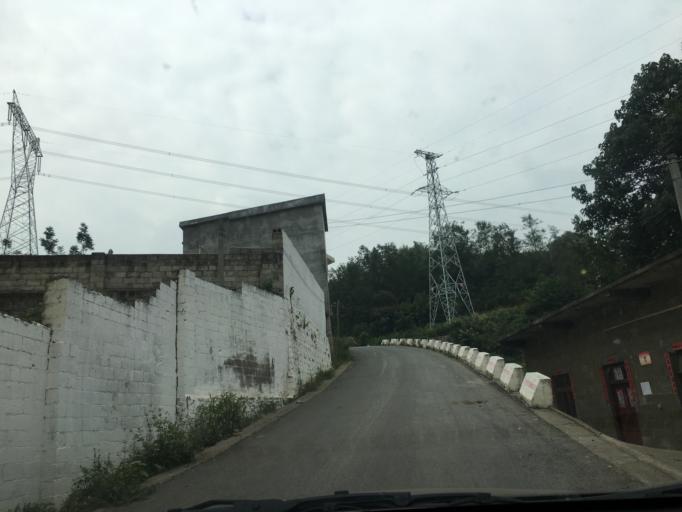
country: CN
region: Guangxi Zhuangzu Zizhiqu
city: Xinzhou
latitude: 25.5391
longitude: 105.5886
